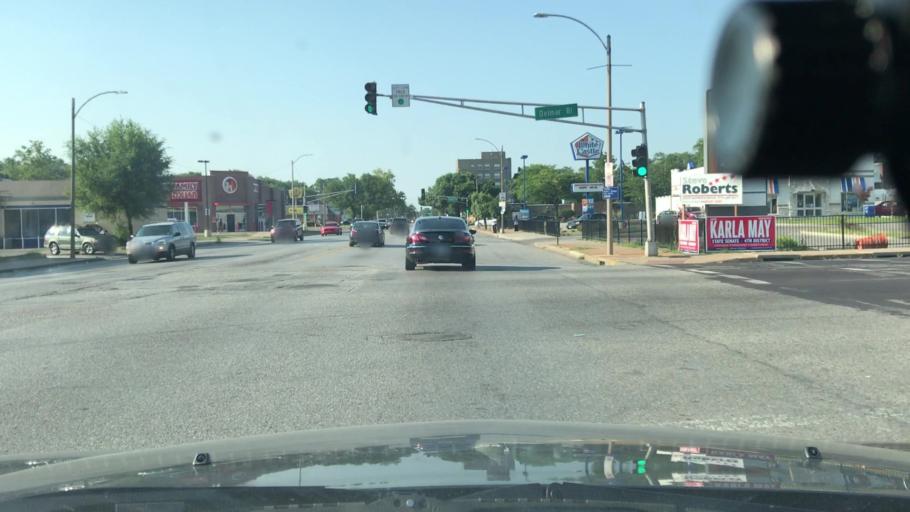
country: US
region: Missouri
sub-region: Saint Louis County
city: Hillsdale
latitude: 38.6515
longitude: -90.2635
